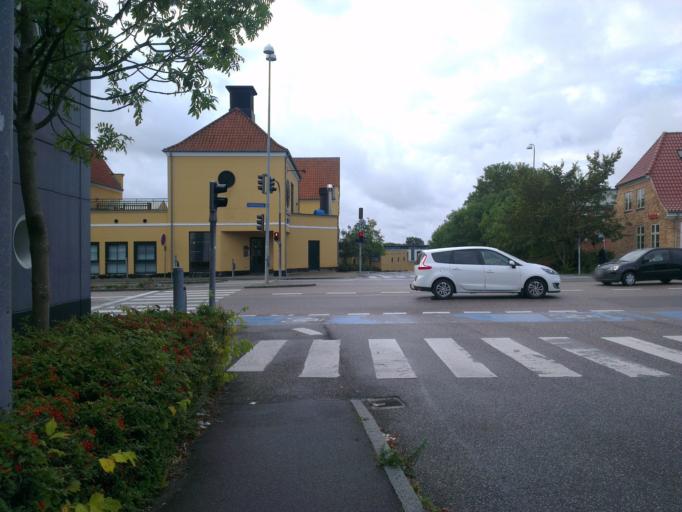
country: DK
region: Capital Region
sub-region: Hillerod Kommune
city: Hillerod
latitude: 55.9298
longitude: 12.2979
